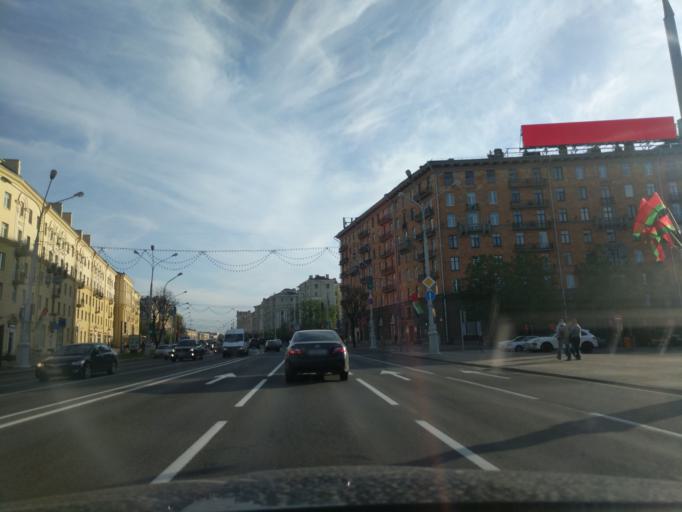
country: BY
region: Minsk
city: Minsk
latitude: 53.9145
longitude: 27.5819
